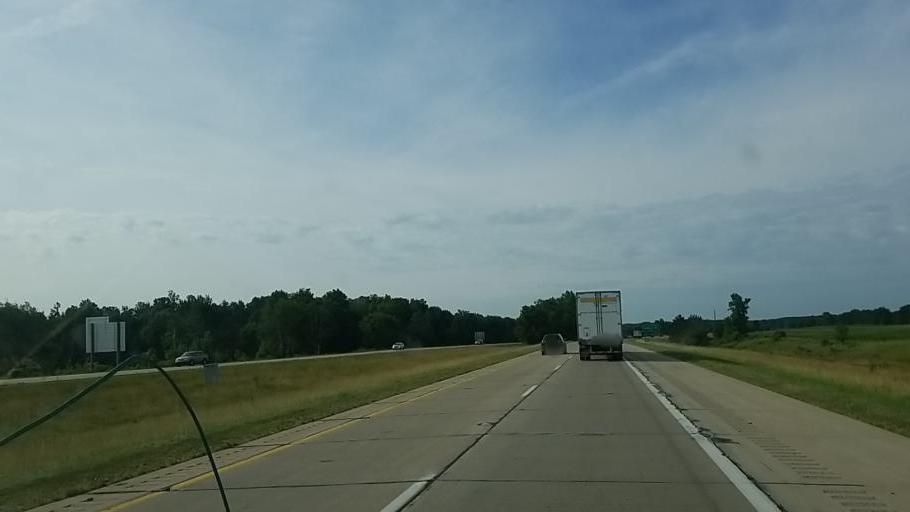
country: US
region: Michigan
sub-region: Eaton County
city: Charlotte
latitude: 42.5344
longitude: -84.8213
